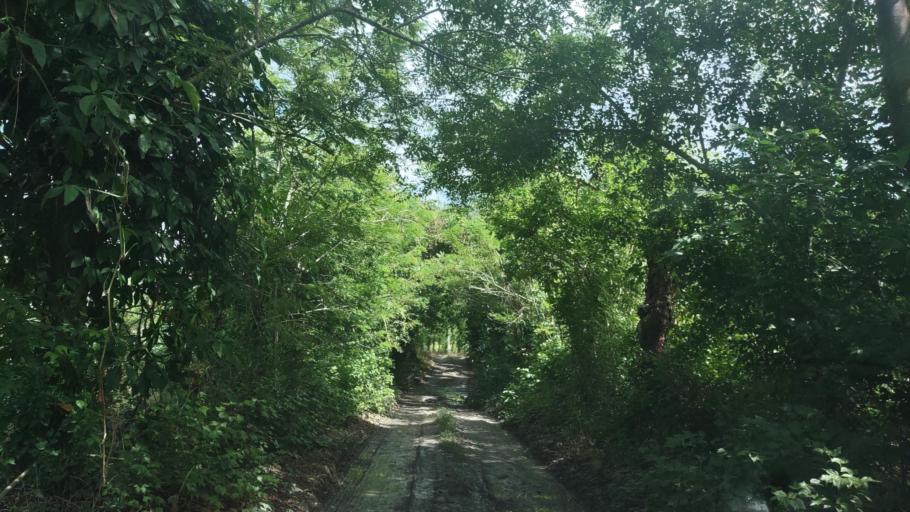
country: MX
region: Veracruz
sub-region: Atzalan
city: Colonias Pedernales
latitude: 20.0599
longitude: -97.0098
